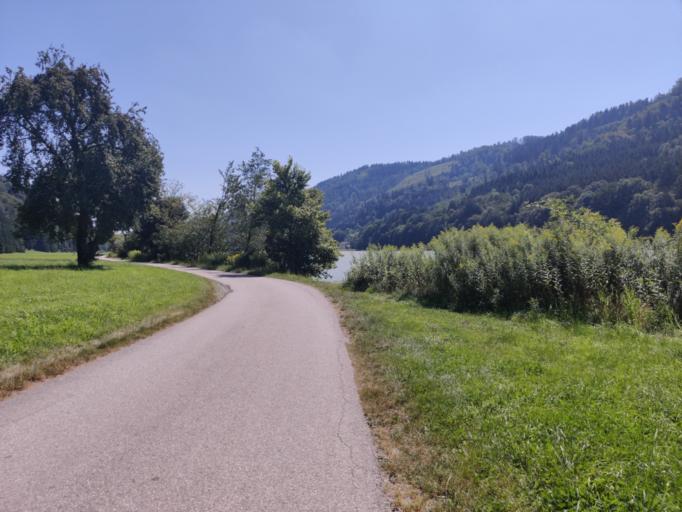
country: AT
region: Upper Austria
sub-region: Politischer Bezirk Rohrbach
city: Pfarrkirchen im Muehlkreis
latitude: 48.4474
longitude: 13.8304
